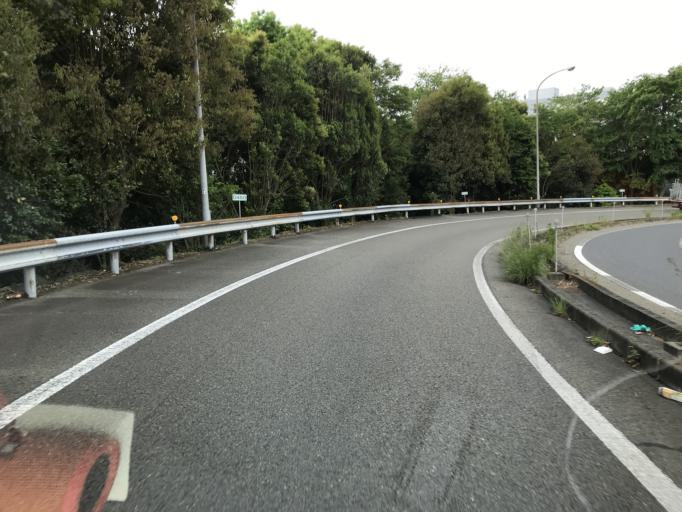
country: JP
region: Kanagawa
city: Hadano
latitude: 35.3511
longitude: 139.2349
